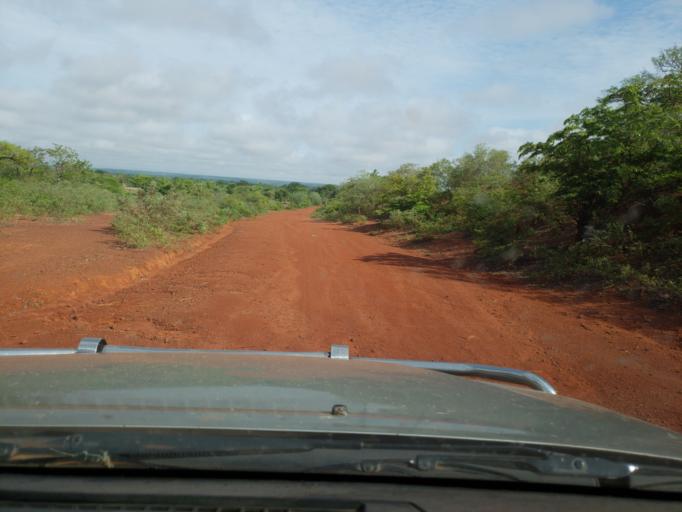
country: ML
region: Sikasso
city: Koutiala
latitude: 12.3890
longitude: -5.9731
